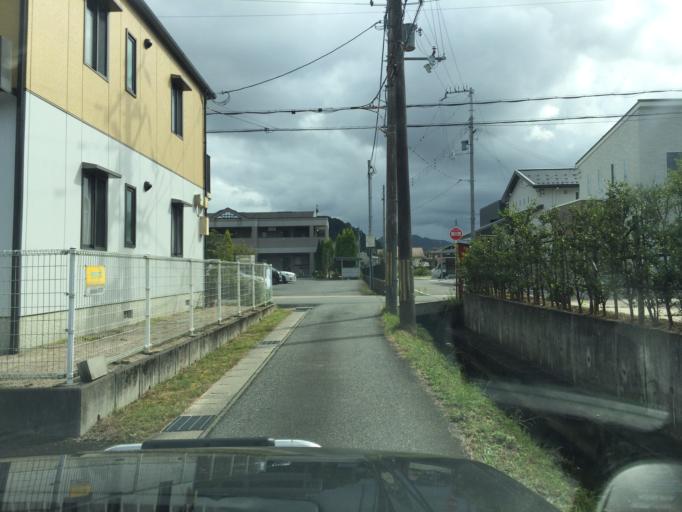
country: JP
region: Hyogo
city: Toyooka
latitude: 35.4764
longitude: 134.7791
